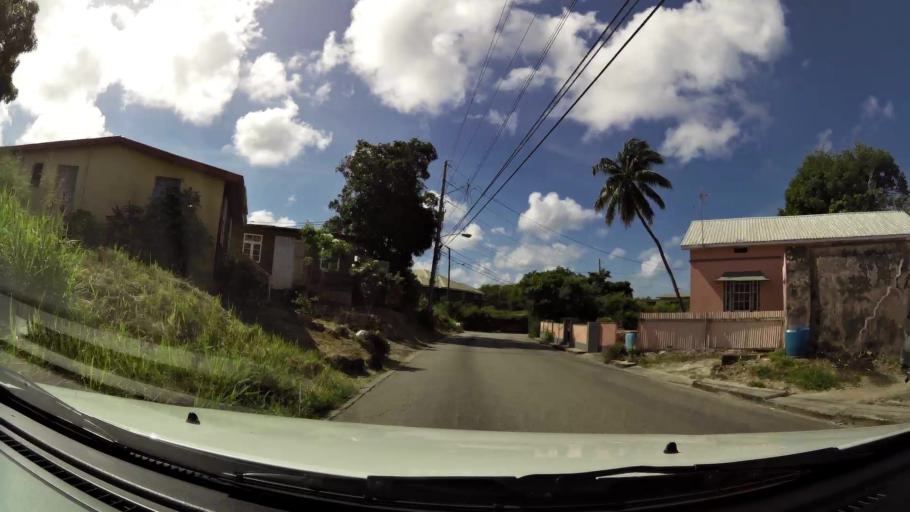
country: BB
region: Saint Peter
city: Speightstown
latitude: 13.2560
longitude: -59.6351
